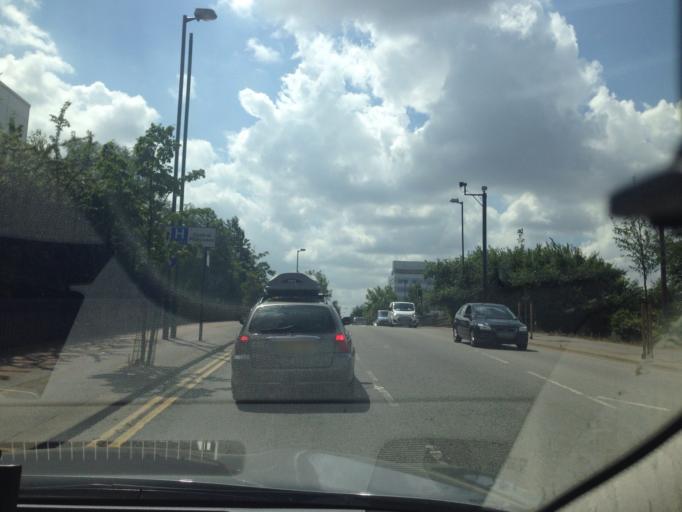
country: GB
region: England
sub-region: Greater London
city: Acton
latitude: 51.5359
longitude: -0.2752
